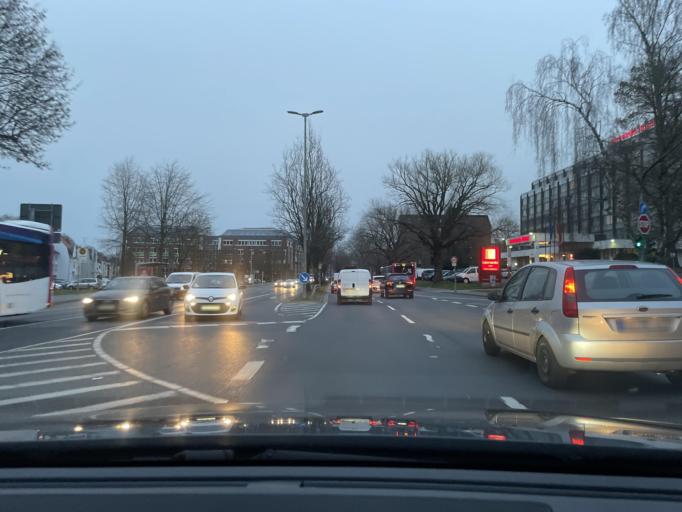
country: DE
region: North Rhine-Westphalia
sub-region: Regierungsbezirk Dusseldorf
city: Monchengladbach
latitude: 51.1912
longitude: 6.4297
